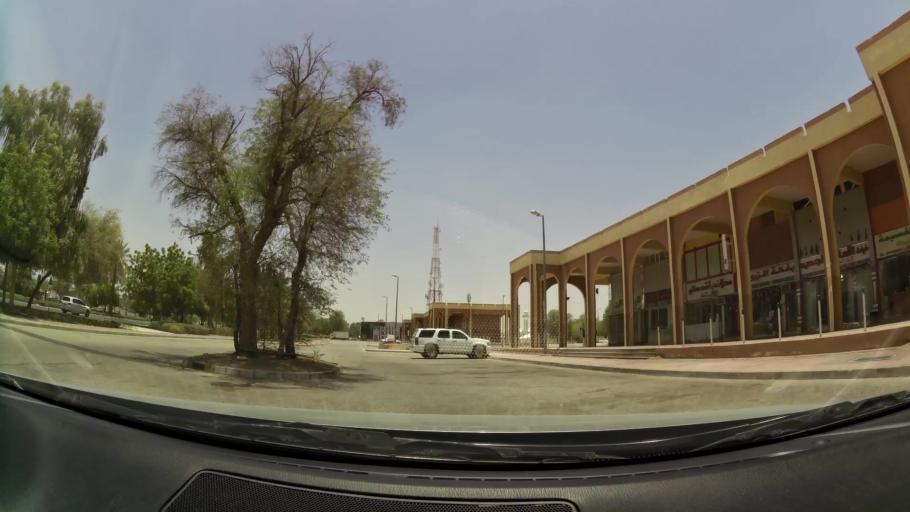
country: OM
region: Al Buraimi
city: Al Buraymi
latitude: 24.2627
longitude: 55.7399
